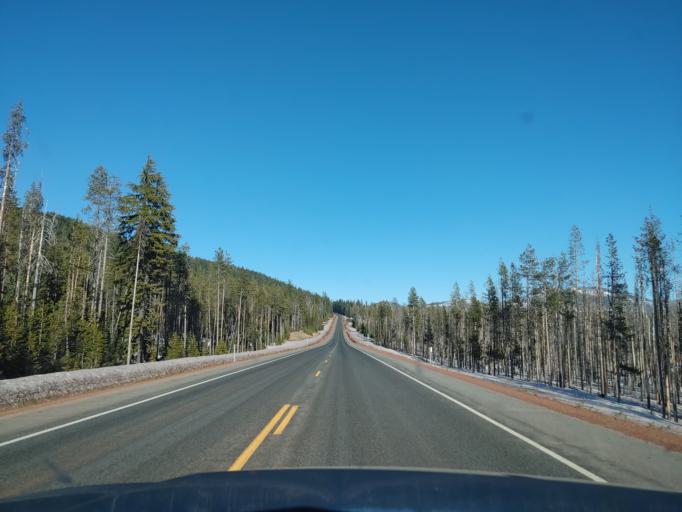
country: US
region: Oregon
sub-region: Lane County
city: Oakridge
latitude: 43.0911
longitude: -122.2337
